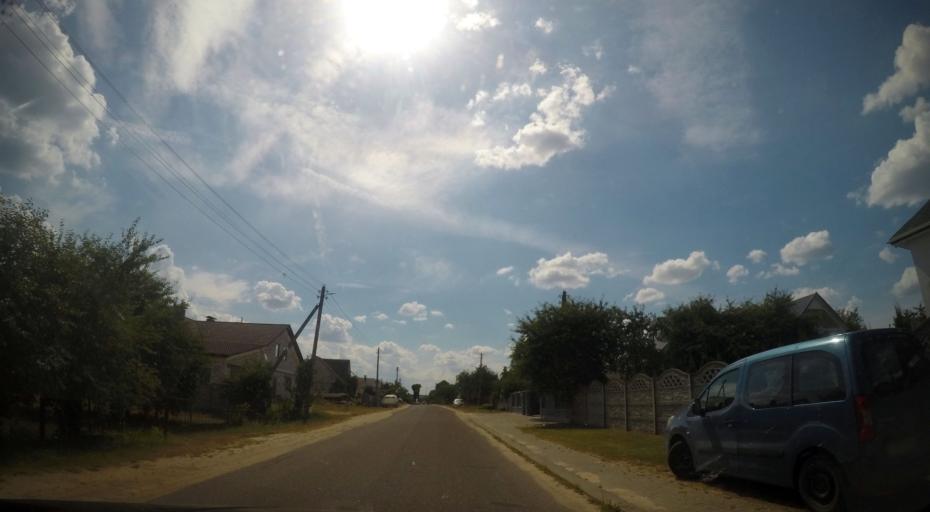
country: BY
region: Grodnenskaya
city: Hrodna
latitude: 53.6325
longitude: 23.8442
